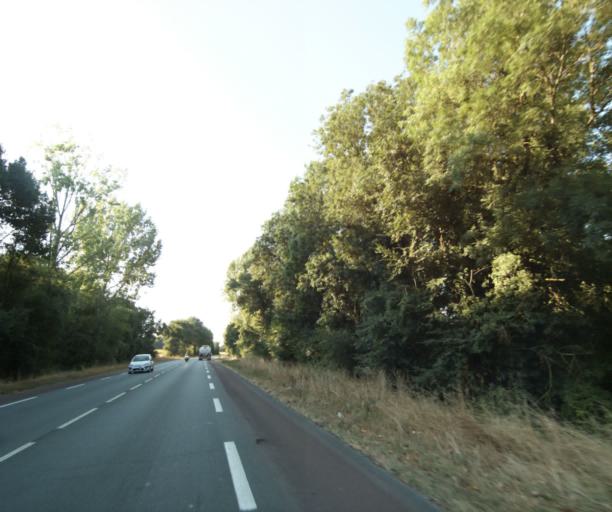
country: FR
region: Poitou-Charentes
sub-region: Departement de la Charente-Maritime
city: Cabariot
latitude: 45.9404
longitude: -0.8642
